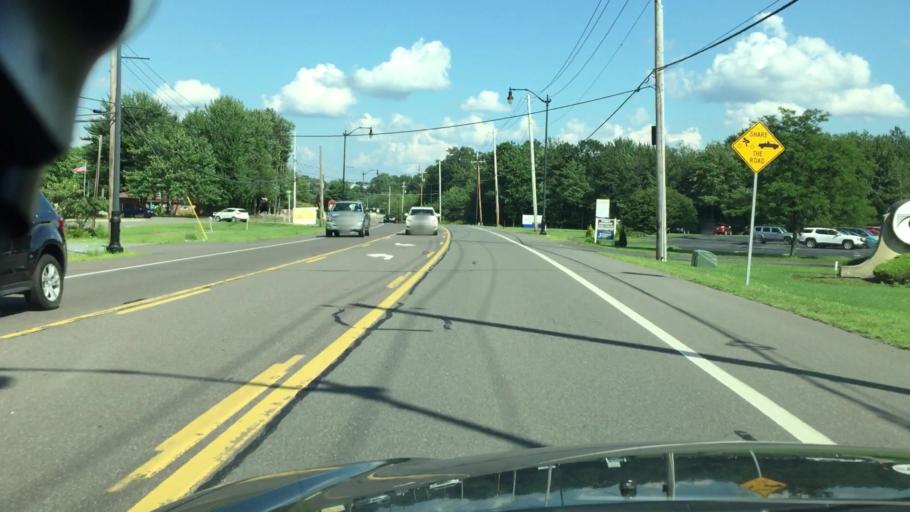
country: US
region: Pennsylvania
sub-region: Luzerne County
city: Hazleton
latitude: 40.9415
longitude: -75.9517
